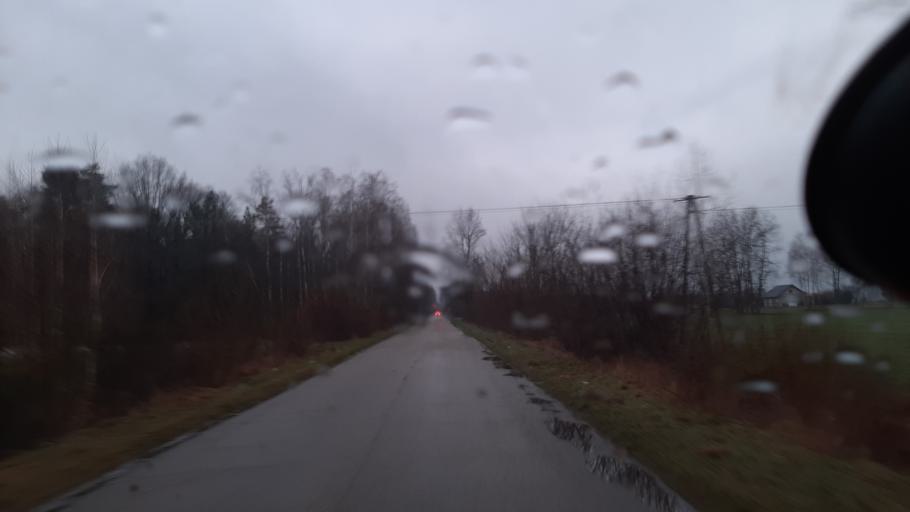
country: PL
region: Lublin Voivodeship
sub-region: Powiat lubartowski
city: Kamionka
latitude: 51.5032
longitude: 22.4883
